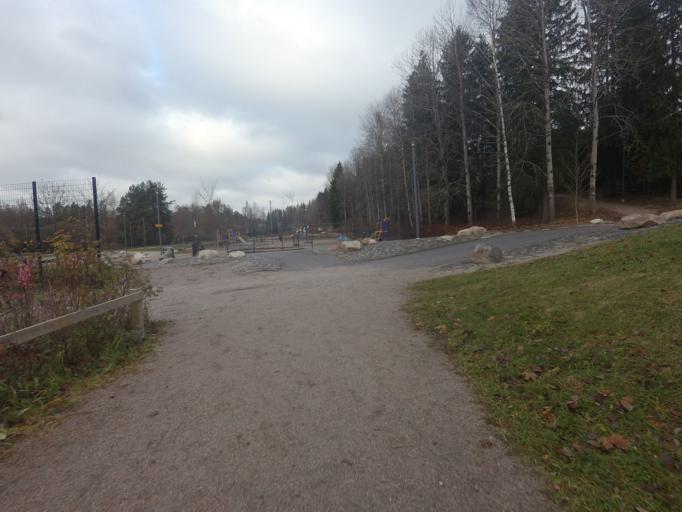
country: FI
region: Uusimaa
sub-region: Helsinki
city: Espoo
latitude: 60.1971
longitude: 24.6777
